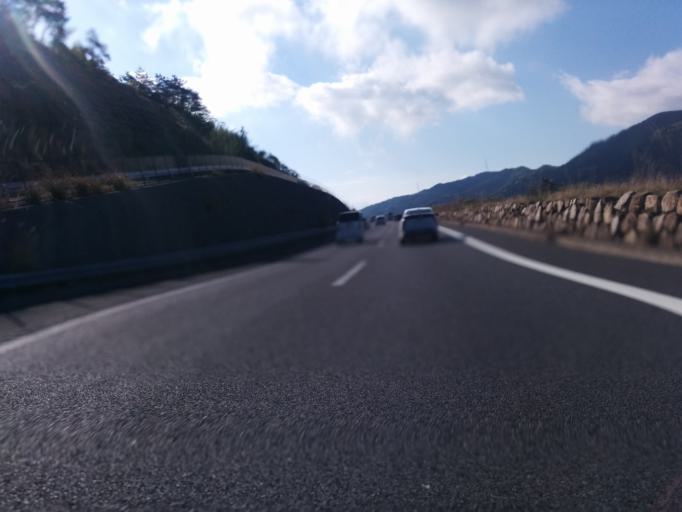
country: JP
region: Shiga Prefecture
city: Kusatsu
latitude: 34.9381
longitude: 136.0364
